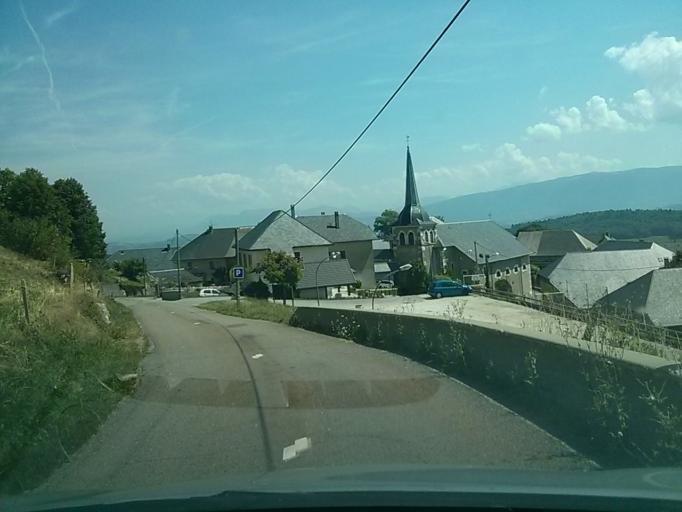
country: FR
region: Rhone-Alpes
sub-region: Departement de la Savoie
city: Chatillon
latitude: 45.7983
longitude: 5.8811
